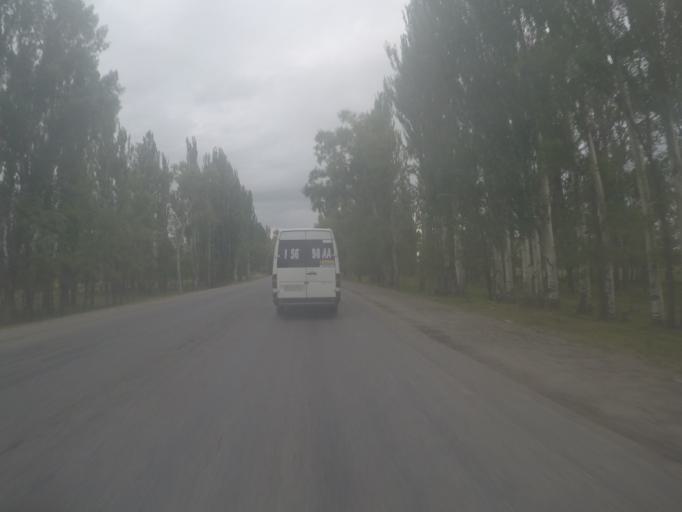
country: KG
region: Ysyk-Koel
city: Karakol
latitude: 42.5471
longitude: 78.3887
